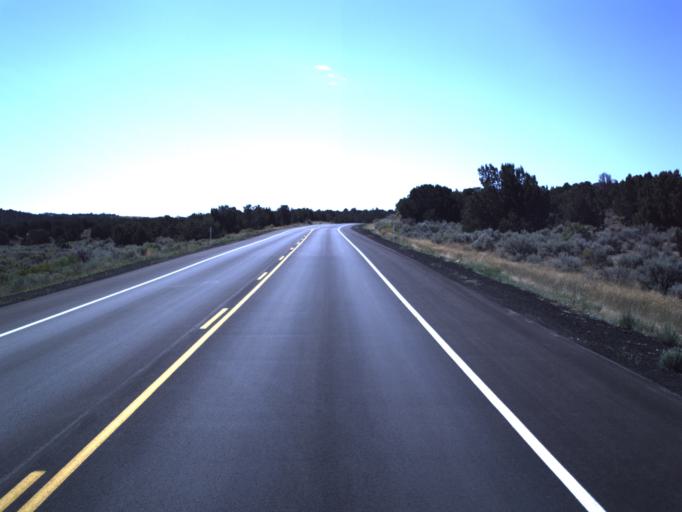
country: US
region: Utah
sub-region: Utah County
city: Eagle Mountain
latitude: 40.0132
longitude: -112.2774
